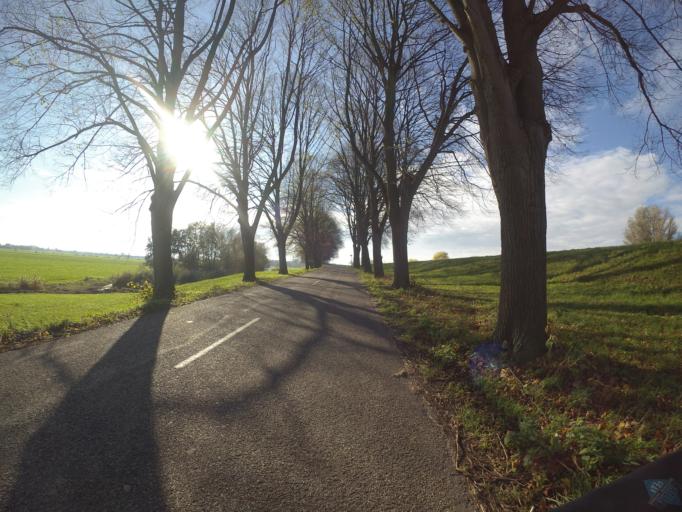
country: NL
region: North Brabant
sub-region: Gemeente Waalwijk
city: Waalwijk
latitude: 51.7215
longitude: 5.0845
